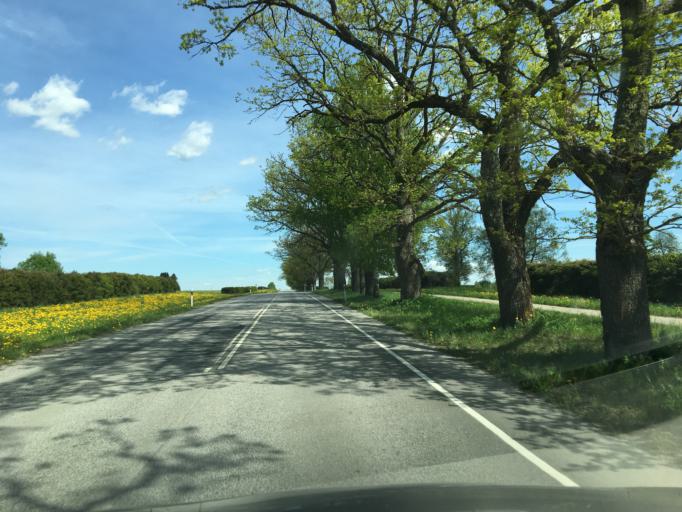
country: EE
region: Vorumaa
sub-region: Antsla vald
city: Vana-Antsla
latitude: 57.9148
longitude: 26.3050
